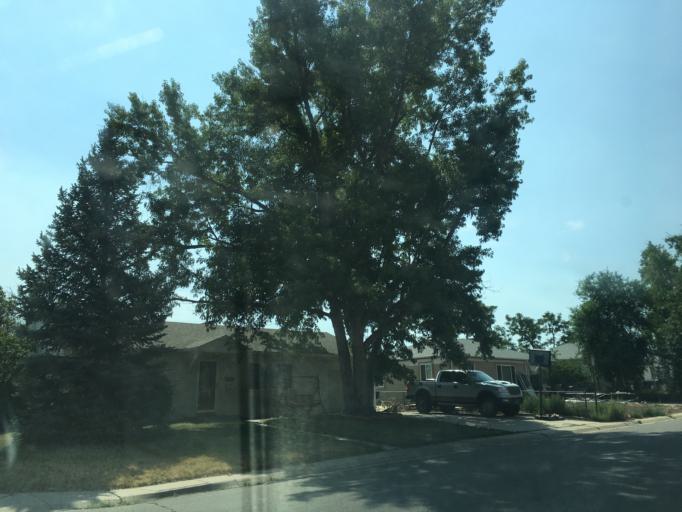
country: US
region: Colorado
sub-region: Jefferson County
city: Lakewood
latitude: 39.6917
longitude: -105.0454
